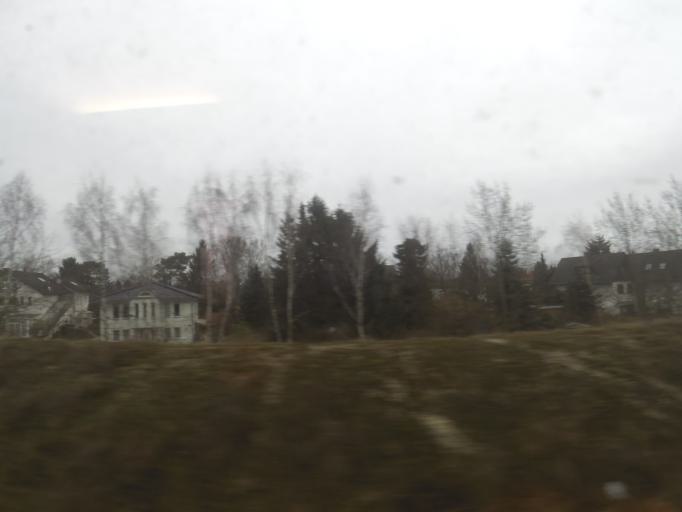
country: DE
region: Berlin
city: Staaken
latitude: 52.5410
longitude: 13.1616
